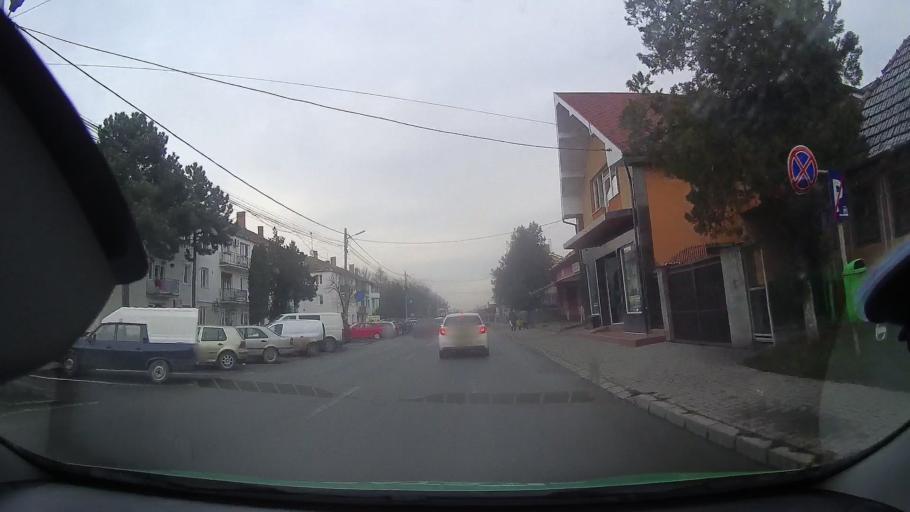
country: RO
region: Mures
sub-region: Comuna Ludus
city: Ludus
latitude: 46.4727
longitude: 24.0954
